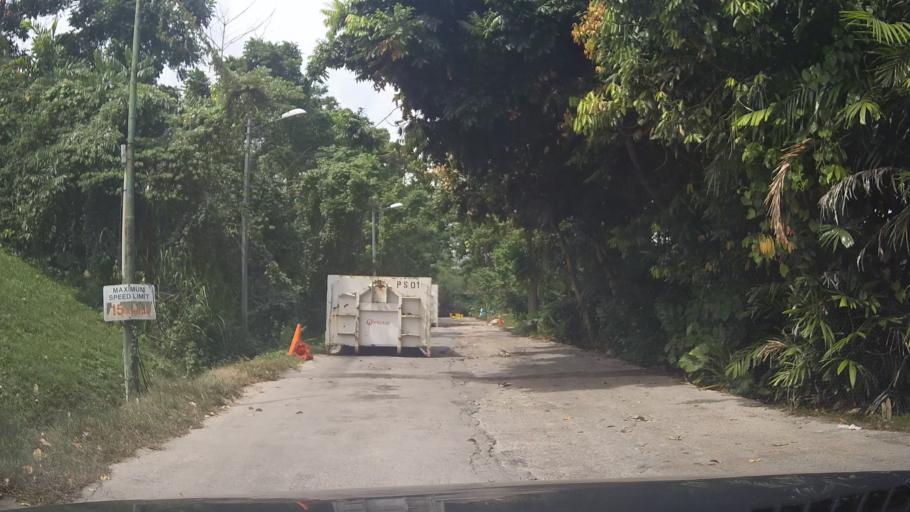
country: MY
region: Johor
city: Kampung Pasir Gudang Baru
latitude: 1.3976
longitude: 103.8623
